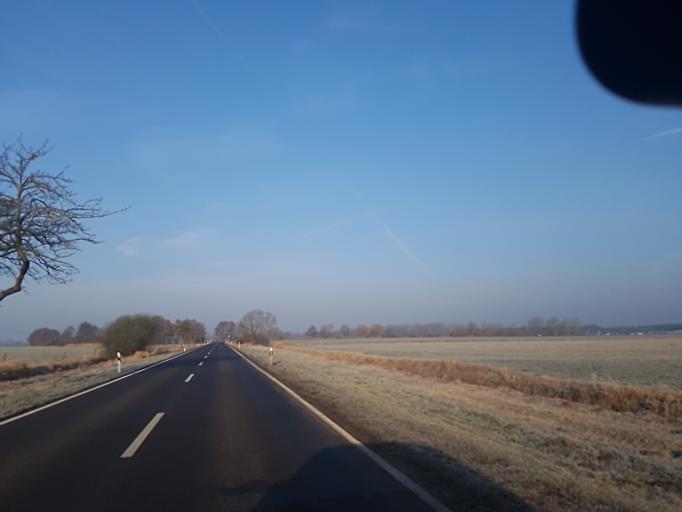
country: DE
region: Brandenburg
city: Bruck
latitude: 52.1993
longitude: 12.7576
